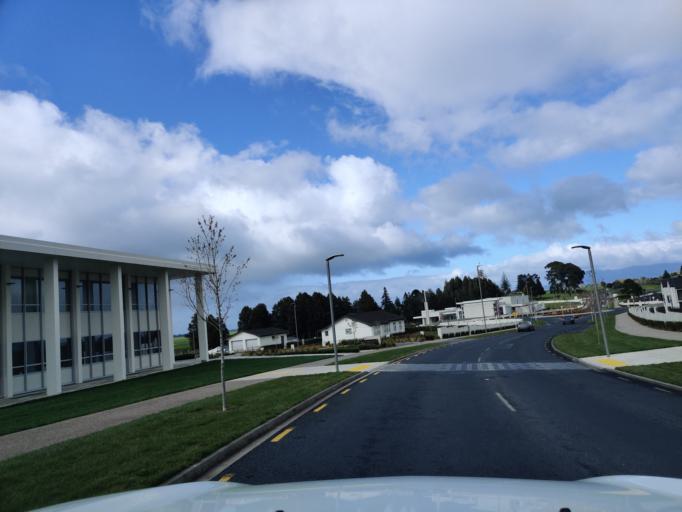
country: NZ
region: Waikato
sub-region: Hamilton City
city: Hamilton
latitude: -37.8208
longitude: 175.2268
